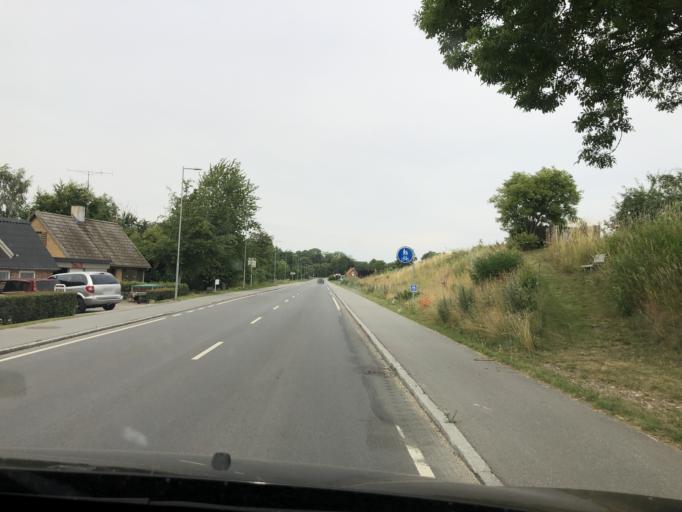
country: DK
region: South Denmark
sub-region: Assens Kommune
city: Glamsbjerg
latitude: 55.2616
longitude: 10.1261
